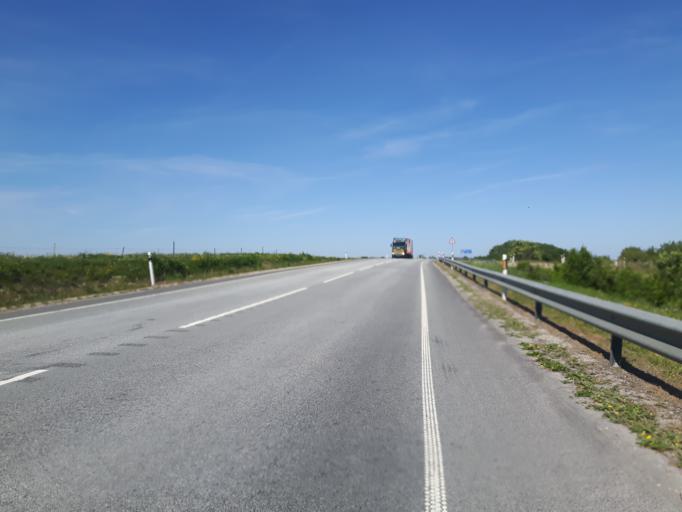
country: EE
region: Ida-Virumaa
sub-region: Aseri vald
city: Aseri
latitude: 59.4323
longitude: 26.9417
